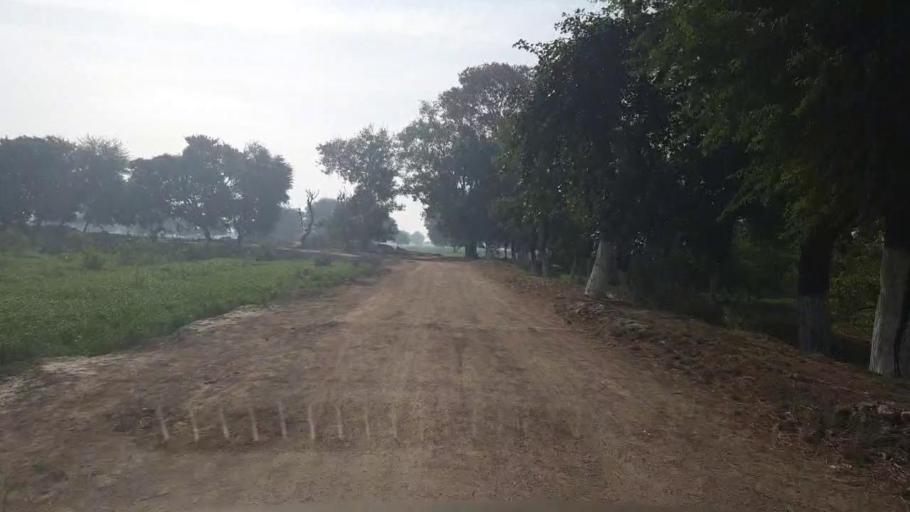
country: PK
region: Sindh
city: Umarkot
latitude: 25.3385
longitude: 69.6870
